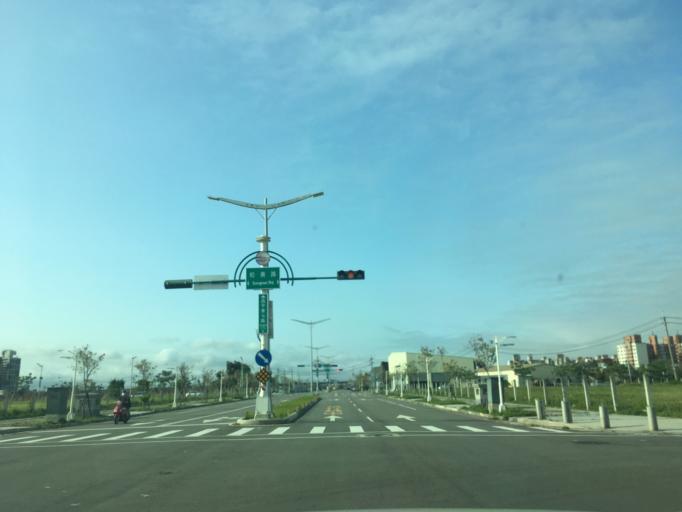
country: TW
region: Taiwan
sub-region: Taichung City
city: Taichung
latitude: 24.1890
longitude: 120.6933
